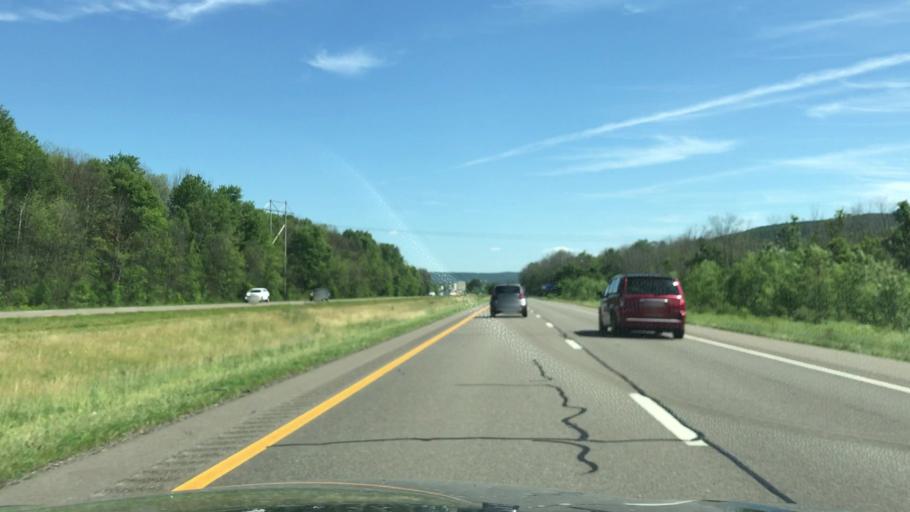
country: US
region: New York
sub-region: Steuben County
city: Gang Mills
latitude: 42.2388
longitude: -77.1947
